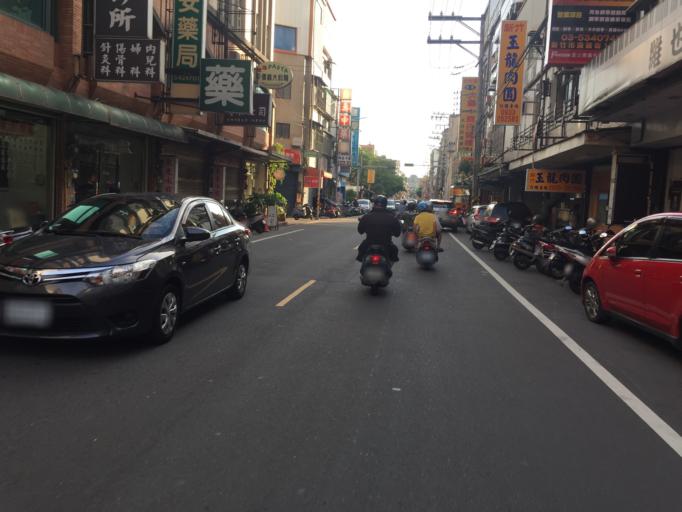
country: TW
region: Taiwan
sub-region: Hsinchu
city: Hsinchu
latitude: 24.8202
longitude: 120.9734
